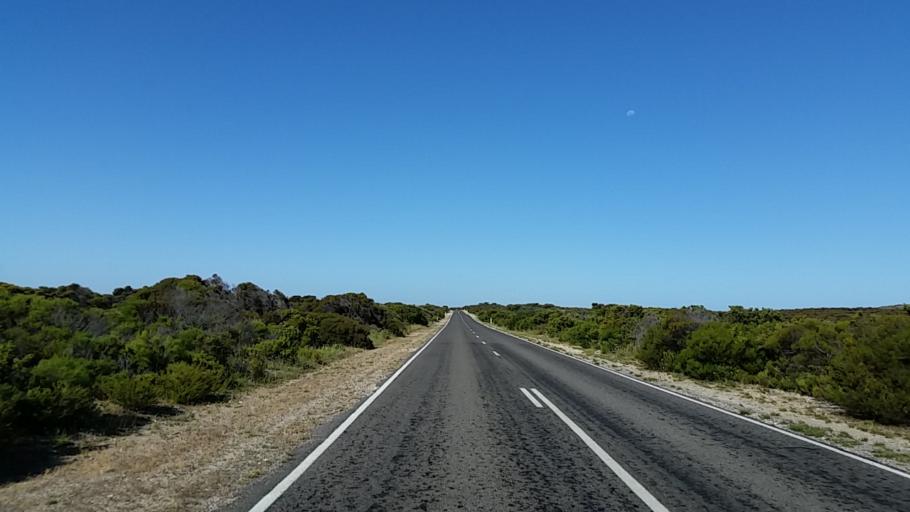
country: AU
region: South Australia
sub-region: Yorke Peninsula
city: Honiton
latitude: -35.2653
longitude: 136.9501
